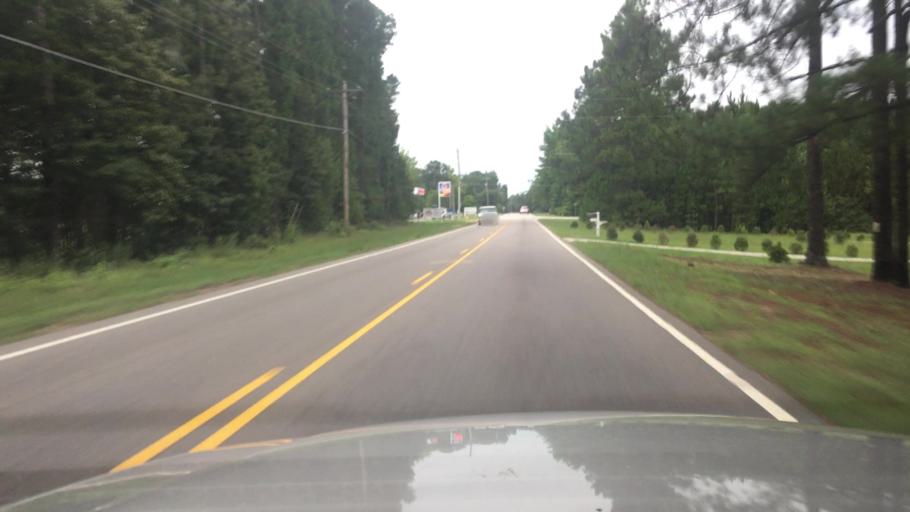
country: US
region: North Carolina
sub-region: Hoke County
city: Rockfish
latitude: 34.9773
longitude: -79.0579
